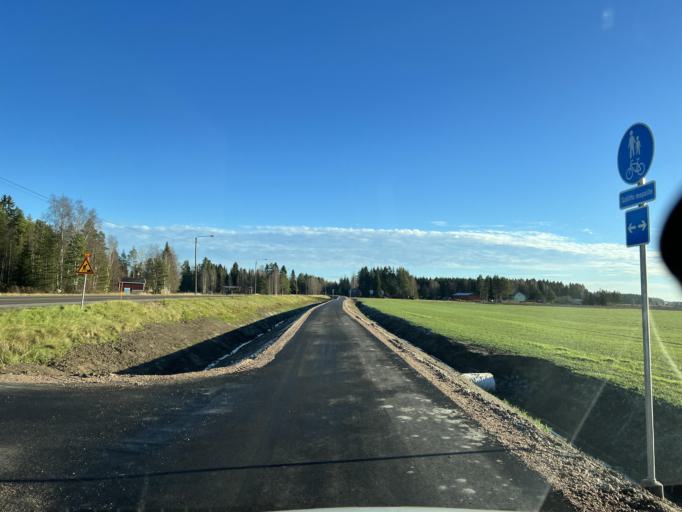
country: FI
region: Northern Ostrobothnia
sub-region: Nivala-Haapajaervi
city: Nivala
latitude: 63.9511
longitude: 24.9054
